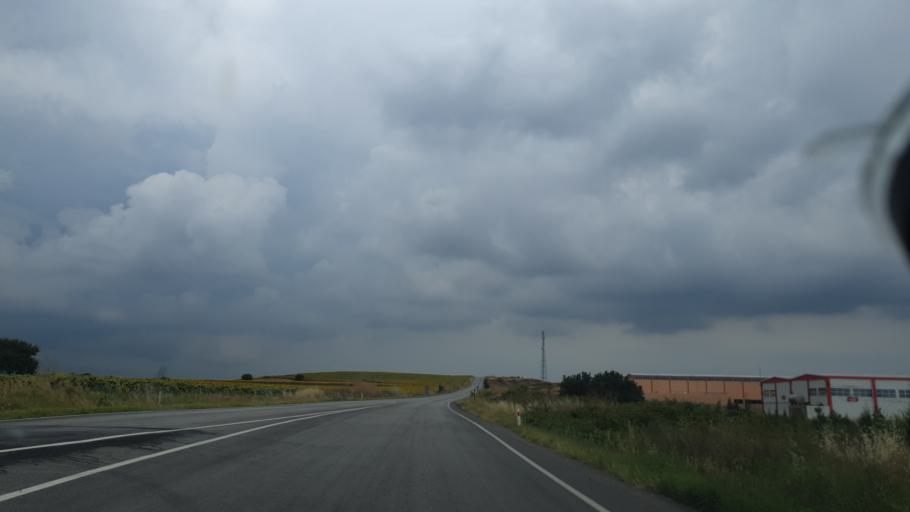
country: TR
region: Tekirdag
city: Hayrabolu
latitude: 41.2228
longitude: 27.0442
